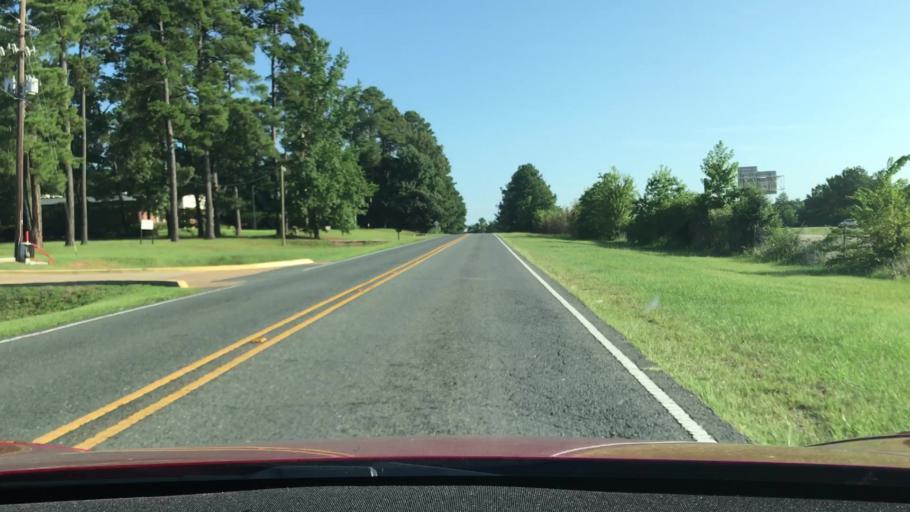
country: US
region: Louisiana
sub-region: Caddo Parish
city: Shreveport
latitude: 32.4478
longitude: -93.8435
